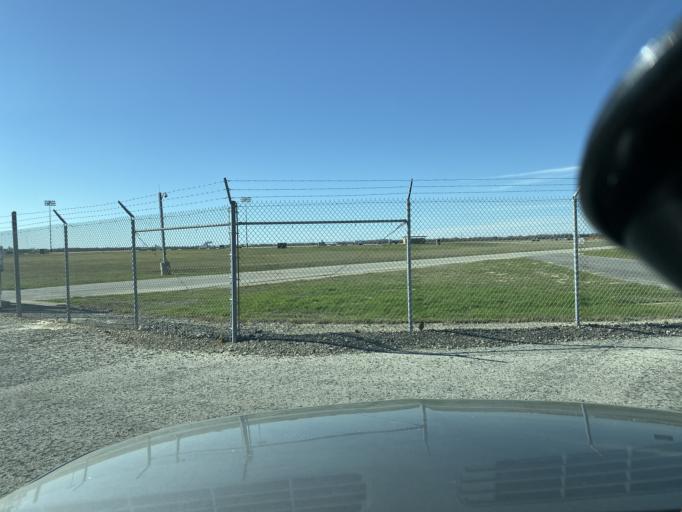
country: US
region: Texas
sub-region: Travis County
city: Hornsby Bend
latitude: 30.1968
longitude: -97.6673
